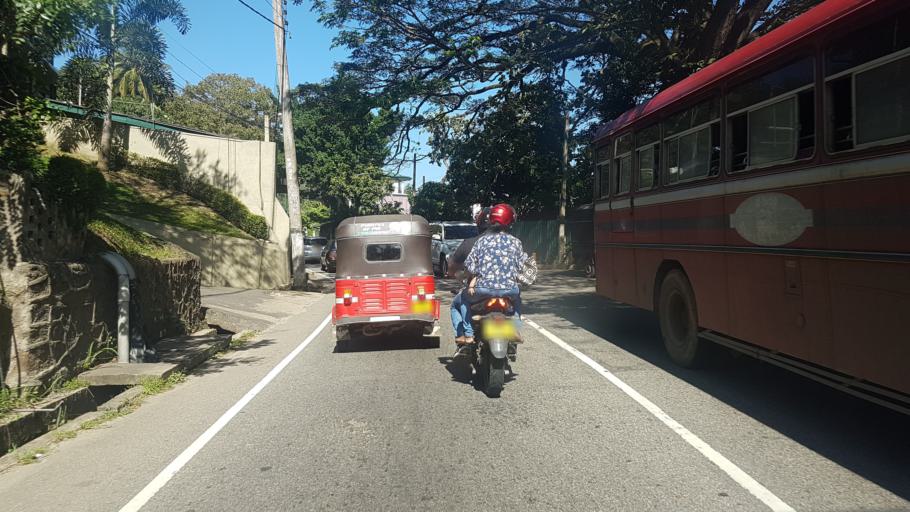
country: LK
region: Central
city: Kandy
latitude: 7.2938
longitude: 80.6526
